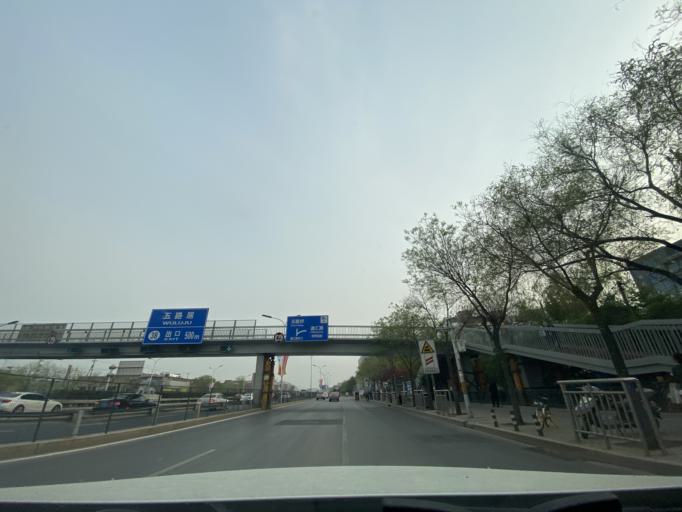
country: CN
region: Beijing
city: Sijiqing
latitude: 39.9405
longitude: 116.2678
